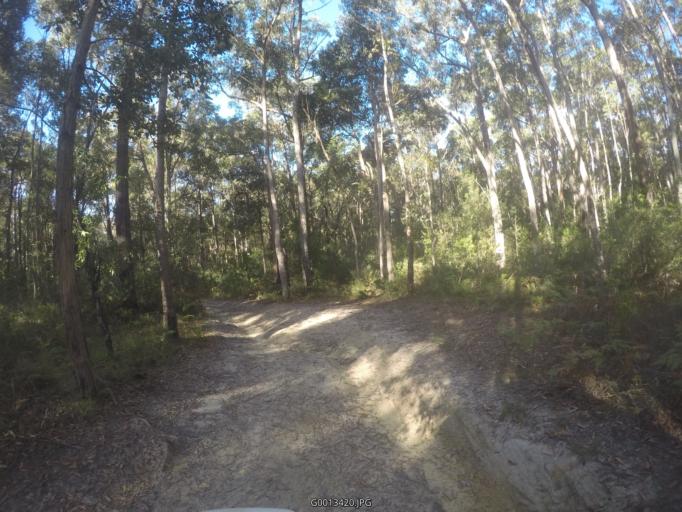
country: AU
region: New South Wales
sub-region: Lake Macquarie Shire
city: Cooranbong
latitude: -33.0680
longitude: 151.3388
